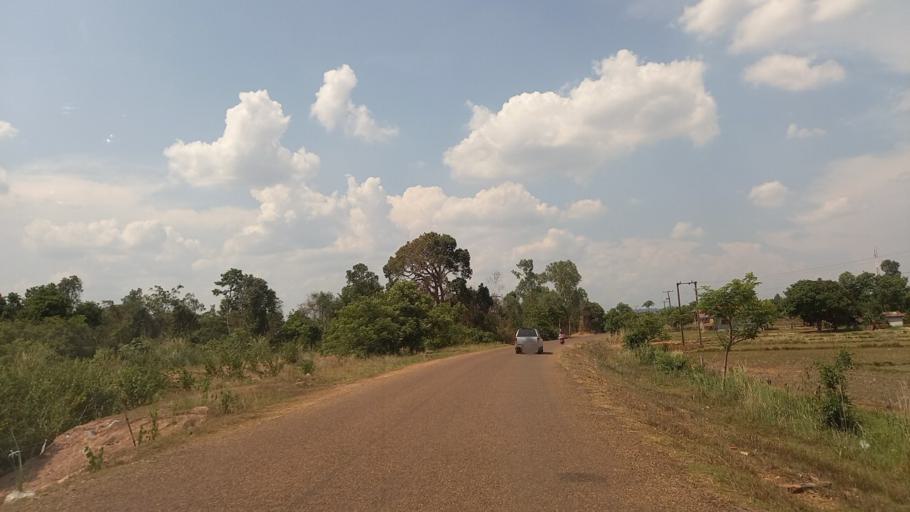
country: LA
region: Bolikhamxai
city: Muang Pakxan
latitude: 18.4218
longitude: 103.7054
